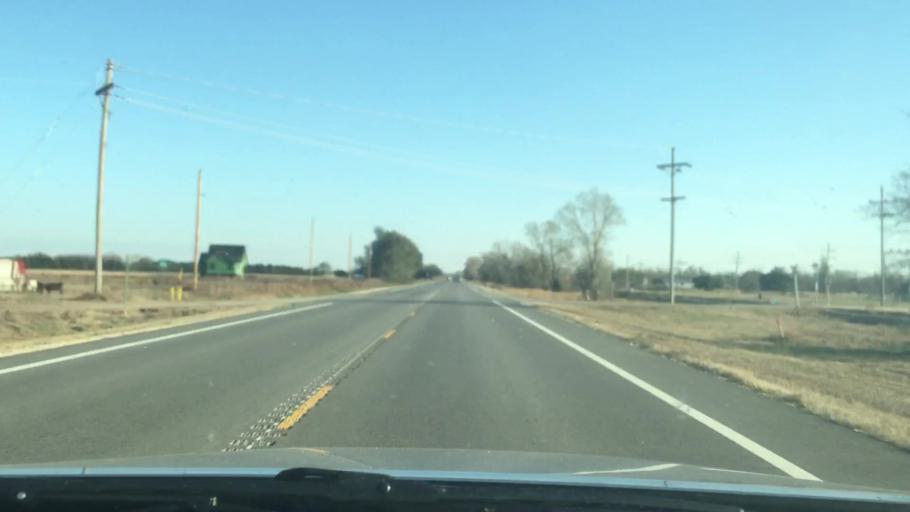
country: US
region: Kansas
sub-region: Reno County
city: Nickerson
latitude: 38.1123
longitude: -98.0324
